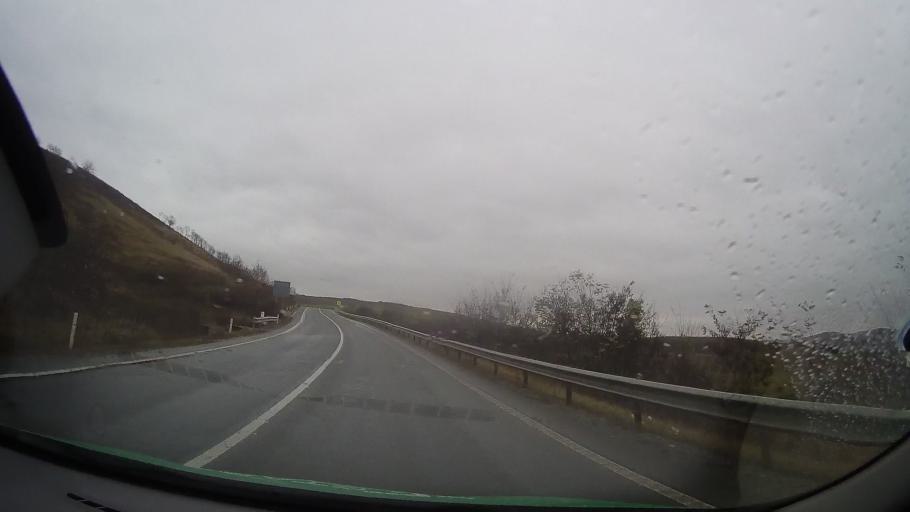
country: RO
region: Bistrita-Nasaud
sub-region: Comuna Teaca
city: Teaca
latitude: 46.9018
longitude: 24.4997
